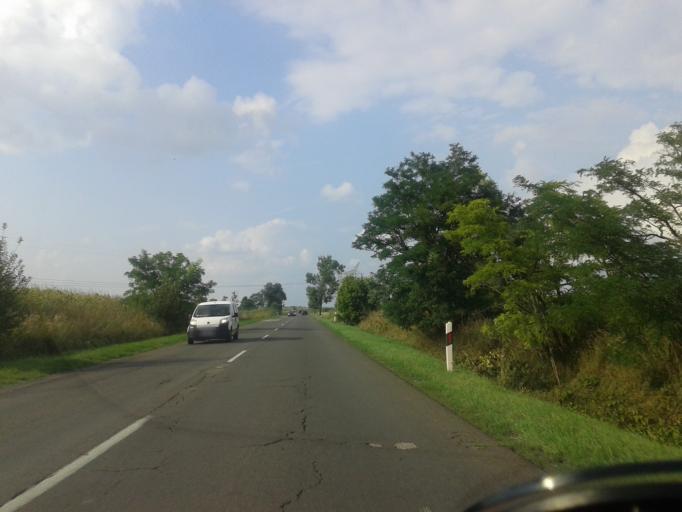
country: HU
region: Bacs-Kiskun
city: Tass
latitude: 47.0428
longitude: 19.0234
